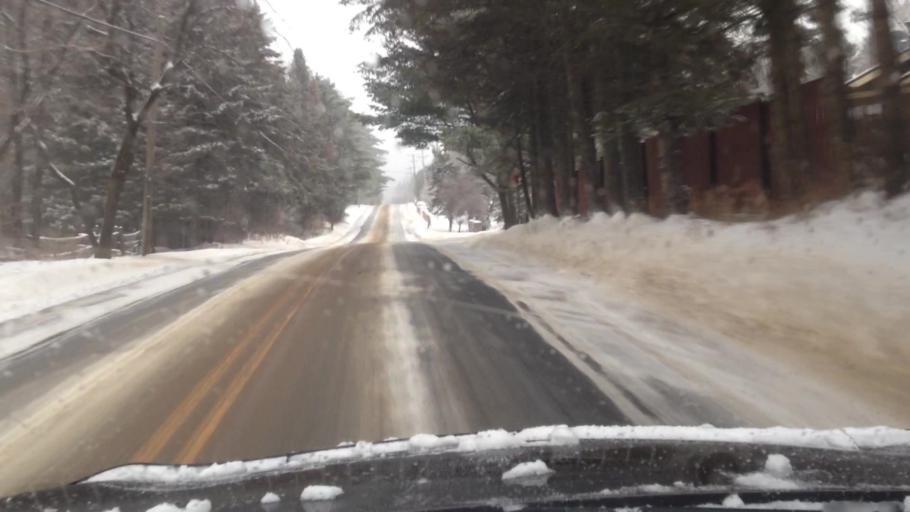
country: CA
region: Quebec
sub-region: Laurentides
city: Mont-Tremblant
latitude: 45.9764
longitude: -74.6141
